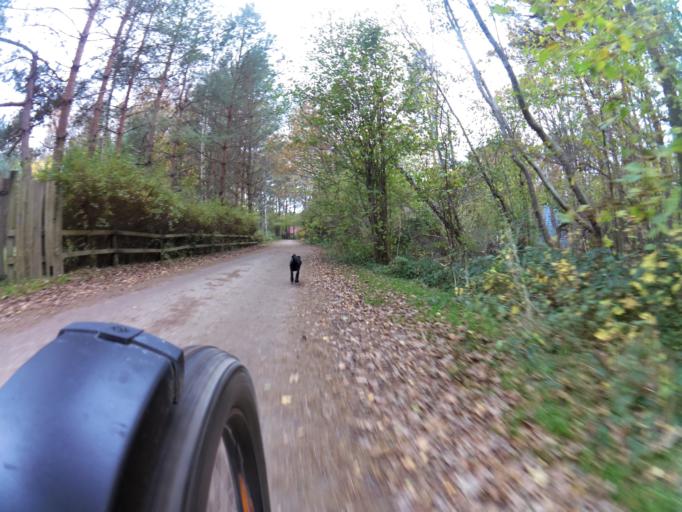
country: PL
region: Pomeranian Voivodeship
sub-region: Powiat pucki
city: Krokowa
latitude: 54.8288
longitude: 18.1073
